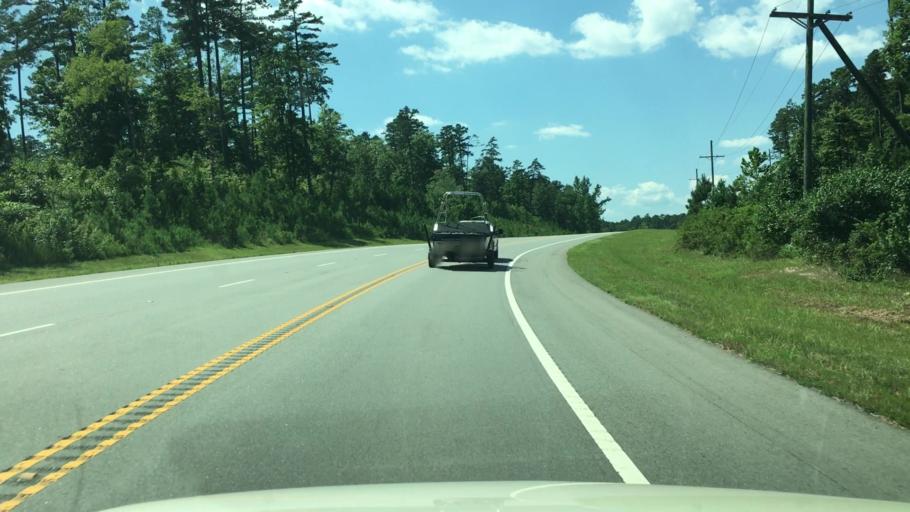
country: US
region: Arkansas
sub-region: Garland County
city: Rockwell
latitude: 34.5188
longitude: -93.3140
